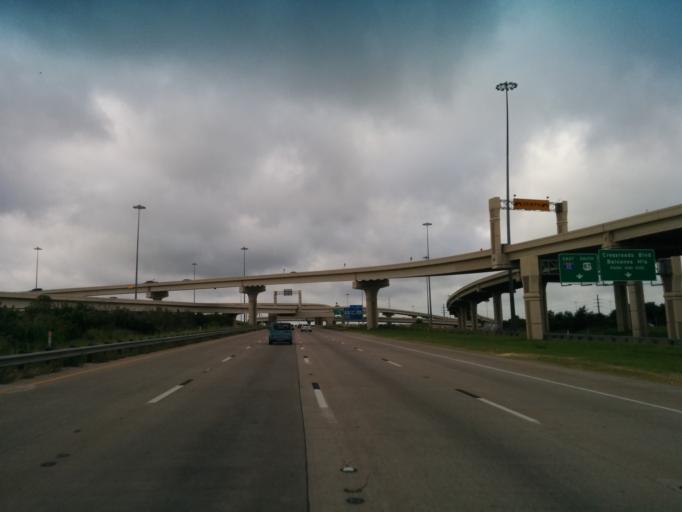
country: US
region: Texas
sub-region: Bexar County
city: Balcones Heights
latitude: 29.5044
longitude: -98.5500
